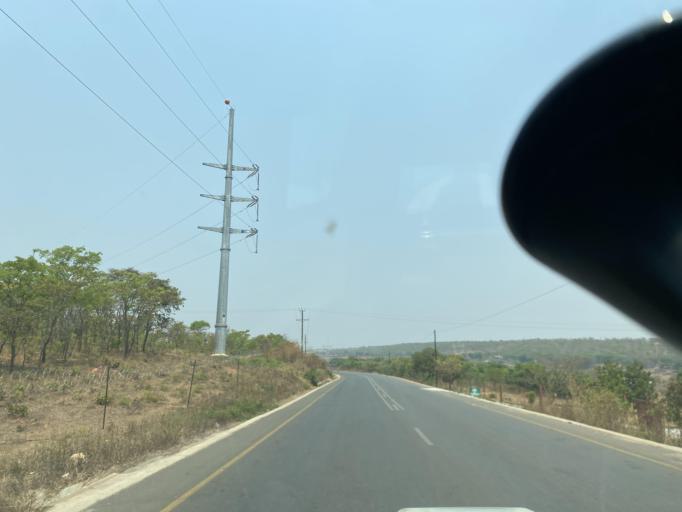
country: ZM
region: Lusaka
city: Lusaka
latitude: -15.5414
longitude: 28.4738
